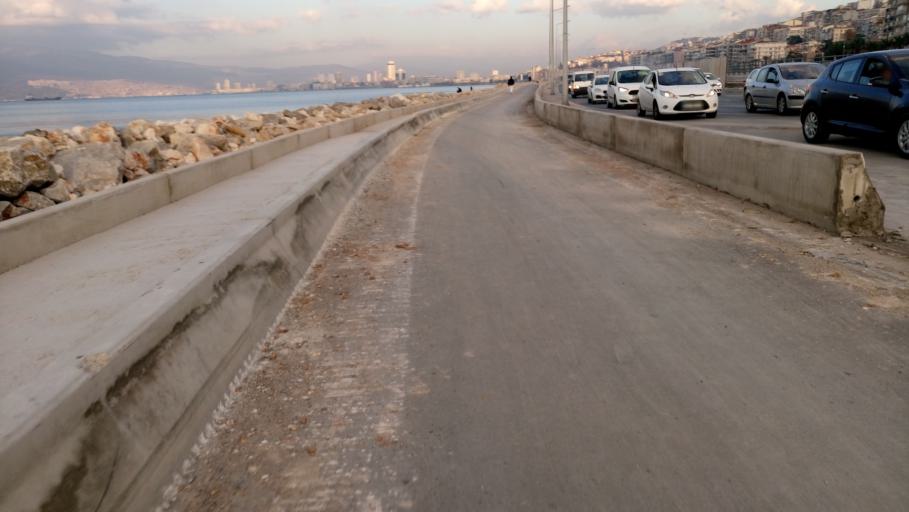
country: TR
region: Izmir
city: Izmir
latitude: 38.4077
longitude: 27.1021
